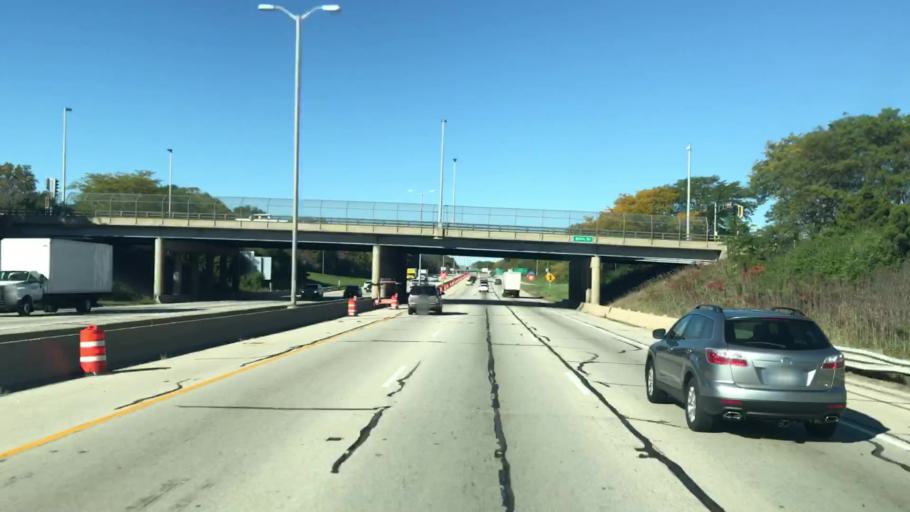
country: US
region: Wisconsin
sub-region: Milwaukee County
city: Greendale
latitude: 42.9624
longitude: -87.9876
